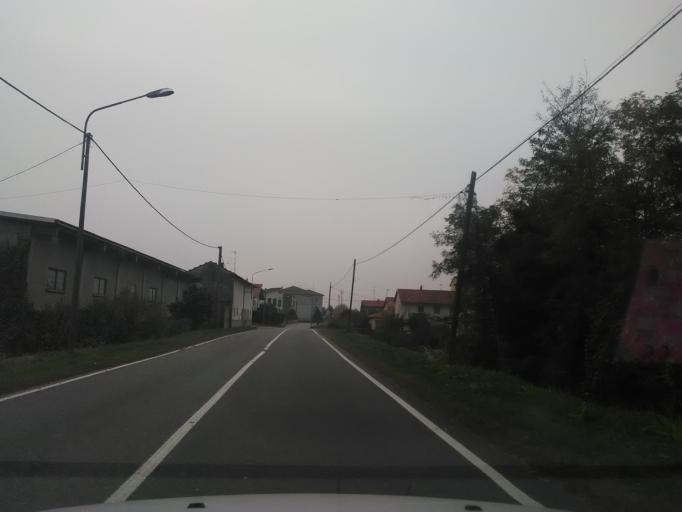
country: IT
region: Piedmont
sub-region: Provincia di Vercelli
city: Bianze
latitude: 45.3068
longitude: 8.1240
